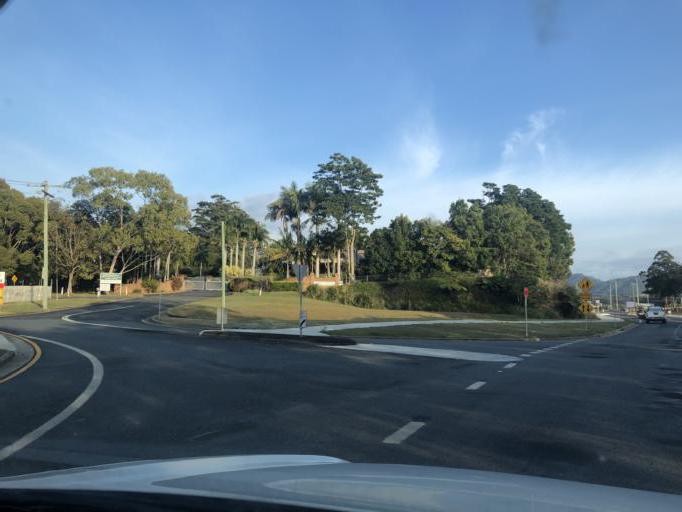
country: AU
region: New South Wales
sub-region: Coffs Harbour
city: Toormina
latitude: -30.3253
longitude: 153.0966
